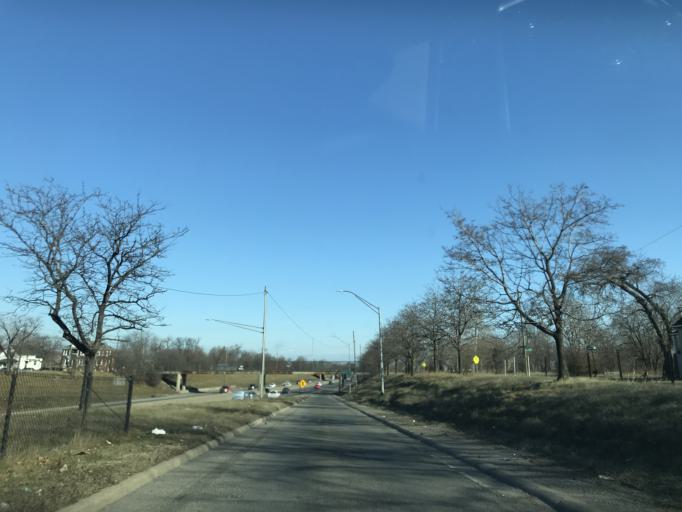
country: US
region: Michigan
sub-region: Wayne County
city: Hamtramck
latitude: 42.3864
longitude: -83.0186
